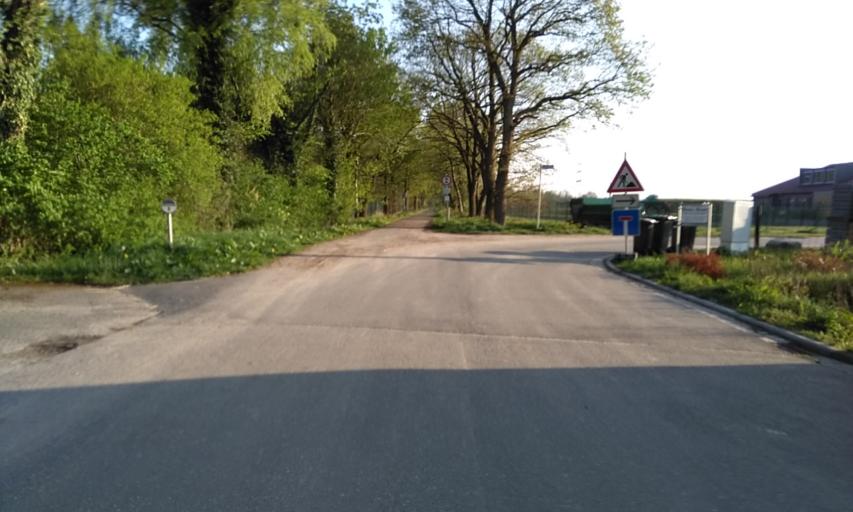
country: DE
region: Lower Saxony
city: Dollern
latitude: 53.5346
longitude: 9.5470
